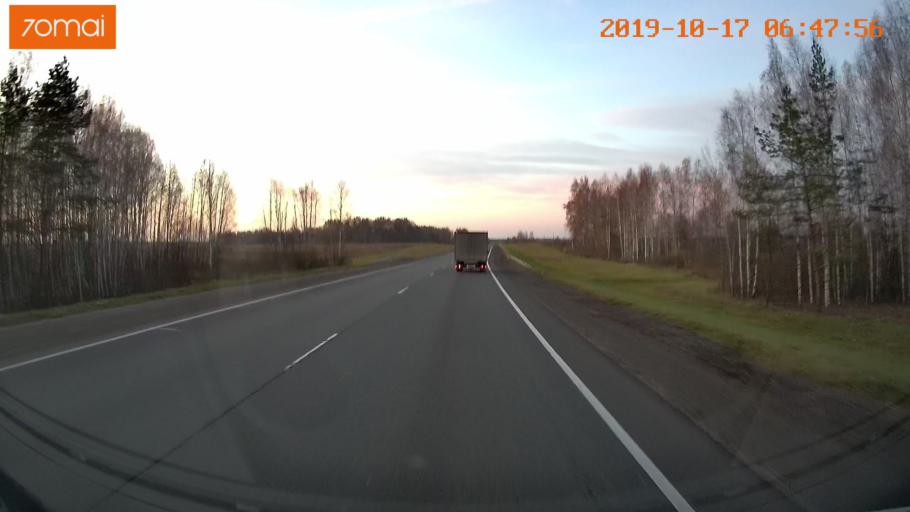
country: RU
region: Vladimir
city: Kideksha
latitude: 56.5296
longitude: 40.5579
